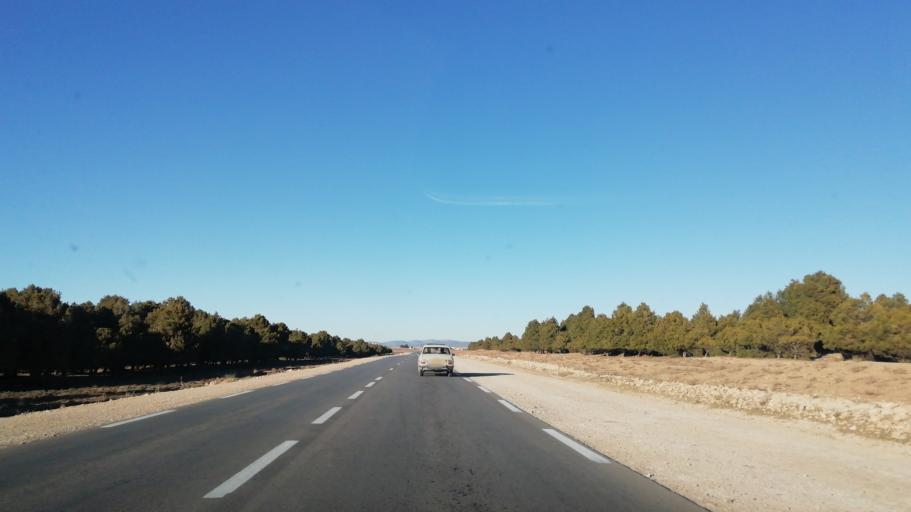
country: DZ
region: Tlemcen
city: Sebdou
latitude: 34.4627
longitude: -1.2748
